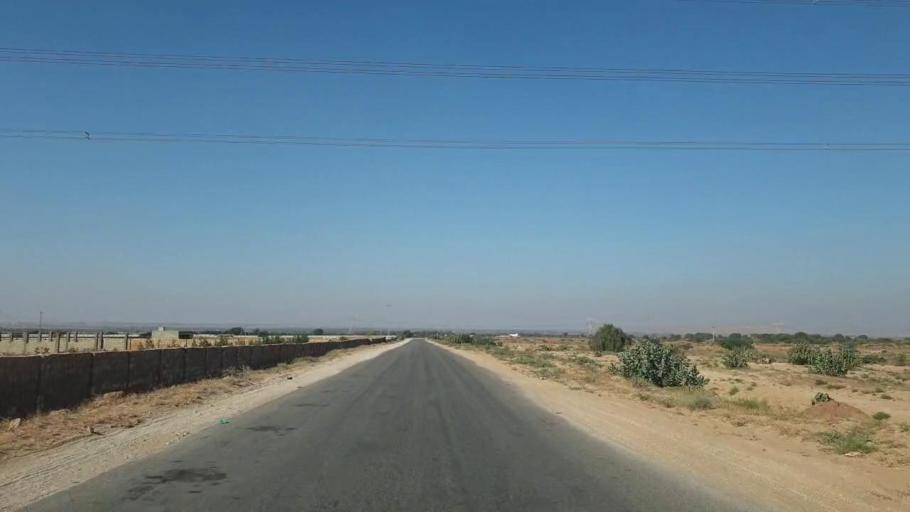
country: PK
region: Sindh
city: Gharo
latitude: 25.1807
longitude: 67.6584
